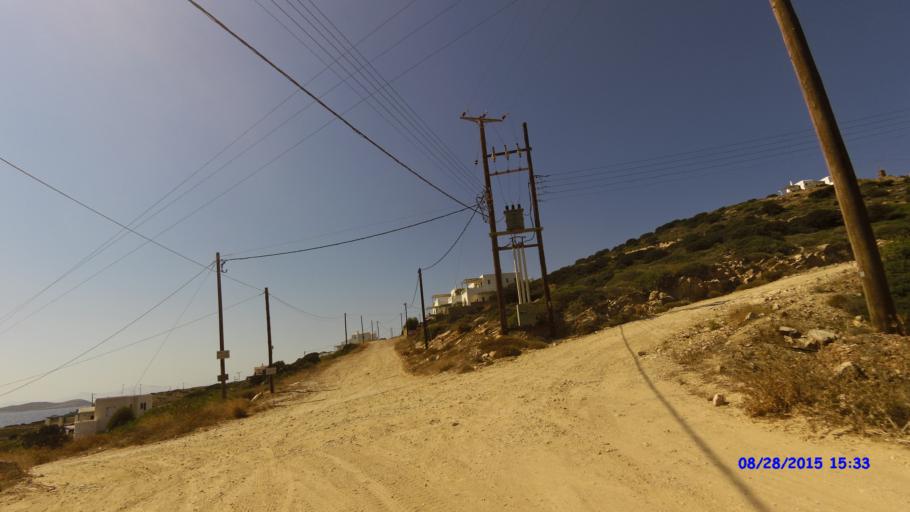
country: GR
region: South Aegean
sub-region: Nomos Kykladon
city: Antiparos
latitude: 36.9798
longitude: 25.0280
